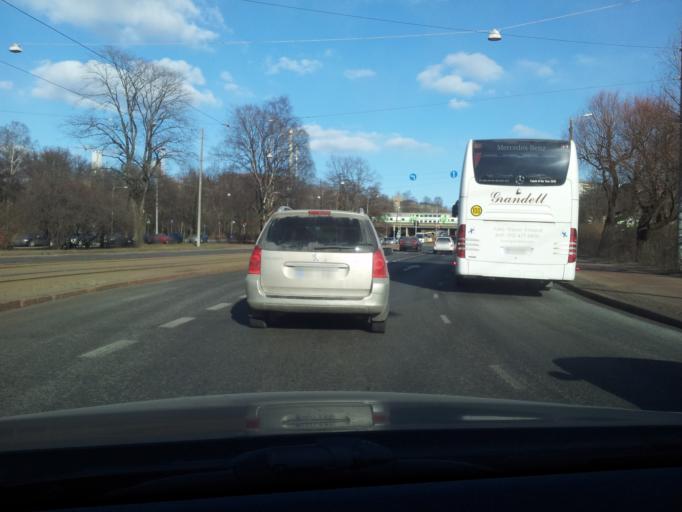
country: FI
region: Uusimaa
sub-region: Helsinki
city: Helsinki
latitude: 60.1848
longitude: 24.9324
